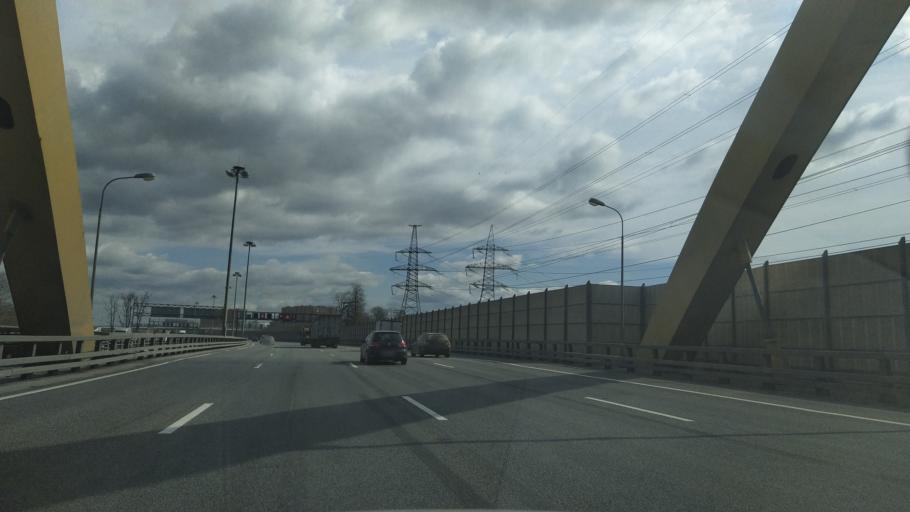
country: RU
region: St.-Petersburg
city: Krasnogvargeisky
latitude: 59.9850
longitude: 30.4935
